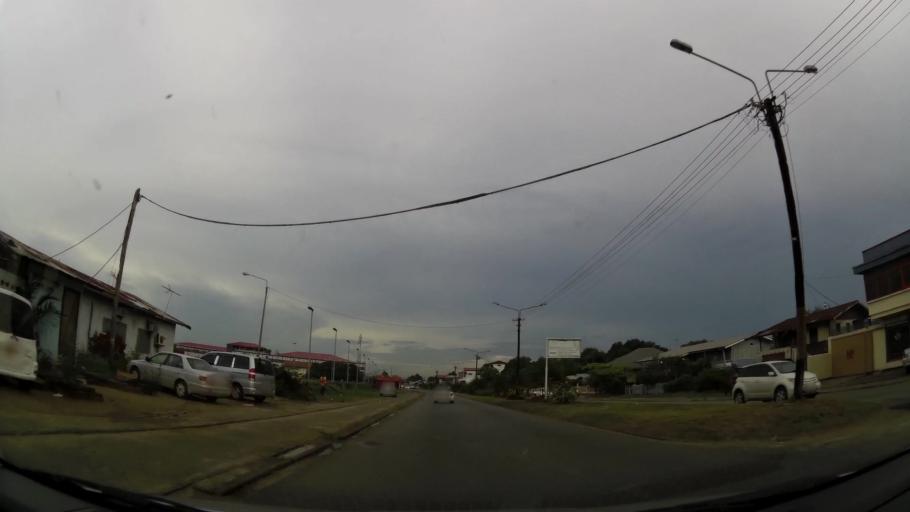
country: SR
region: Paramaribo
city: Paramaribo
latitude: 5.8084
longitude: -55.1877
